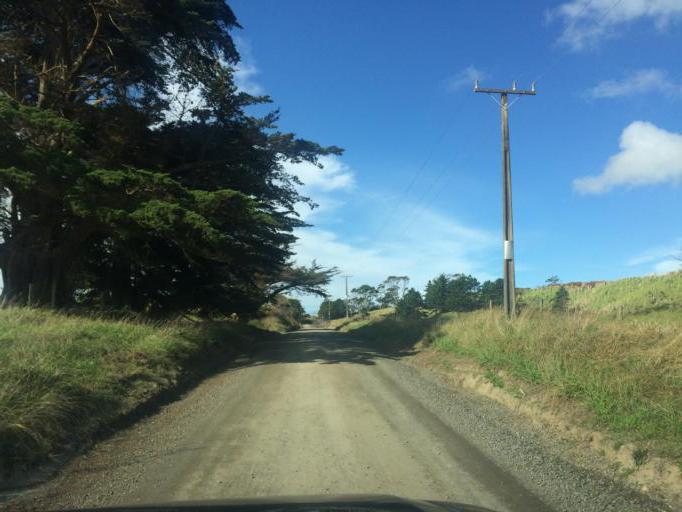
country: NZ
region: Northland
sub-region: Kaipara District
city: Dargaville
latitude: -36.0273
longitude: 173.8737
